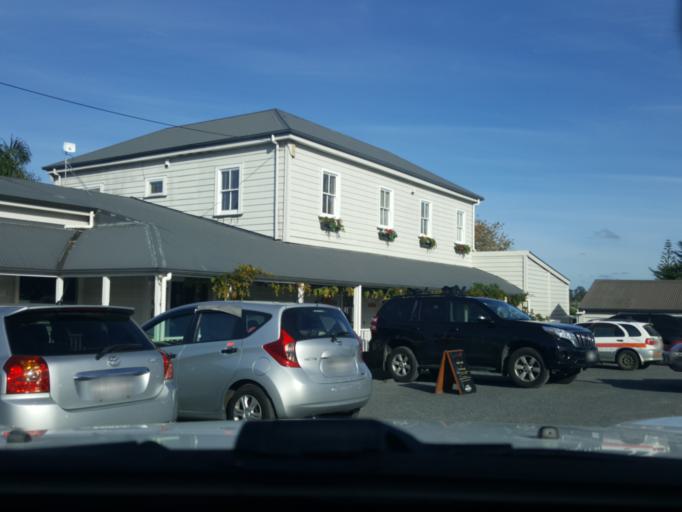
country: NZ
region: Auckland
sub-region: Auckland
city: Rosebank
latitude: -36.7591
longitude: 174.5975
